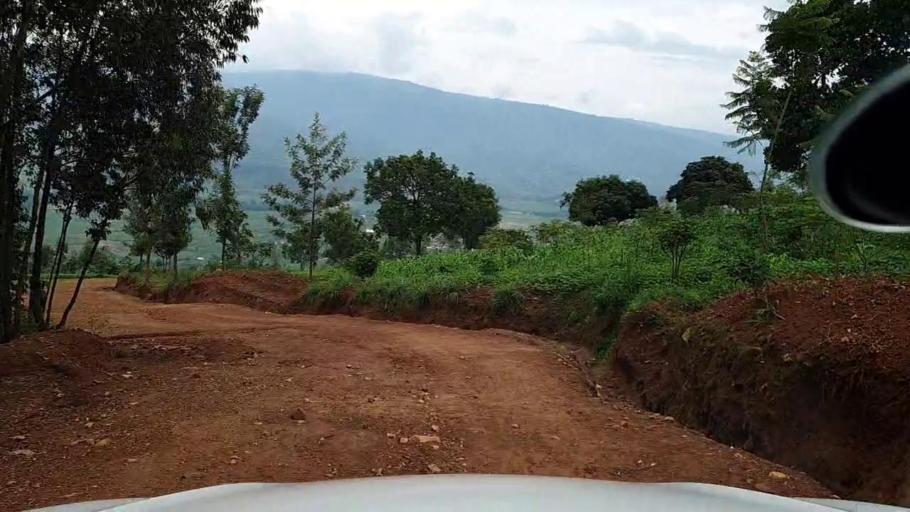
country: RW
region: Kigali
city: Kigali
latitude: -1.8773
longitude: 29.9151
